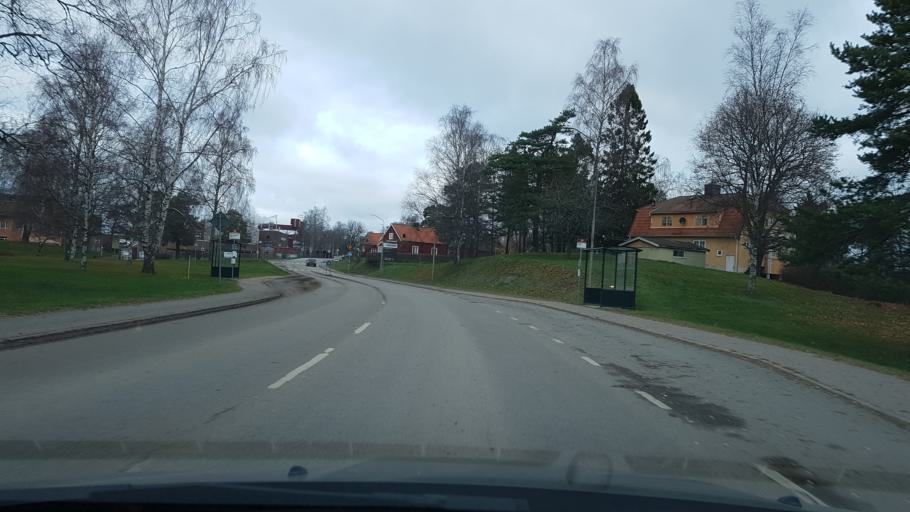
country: SE
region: Stockholm
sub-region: Norrtalje Kommun
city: Hallstavik
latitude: 60.0595
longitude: 18.5967
